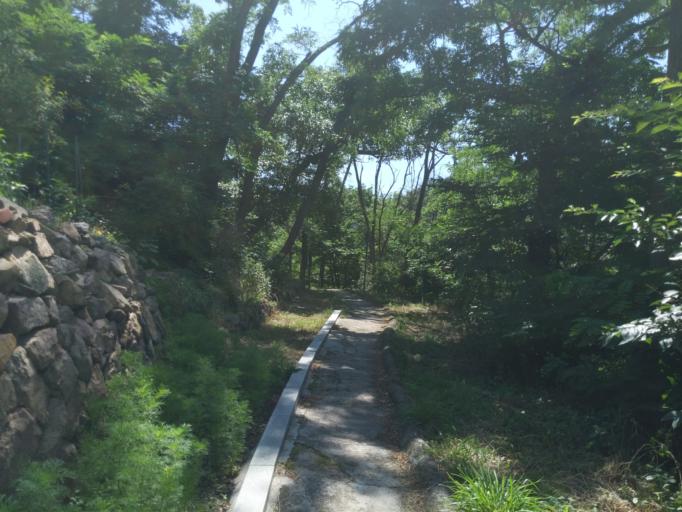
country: KR
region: Seoul
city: Seoul
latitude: 37.6017
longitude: 126.9635
